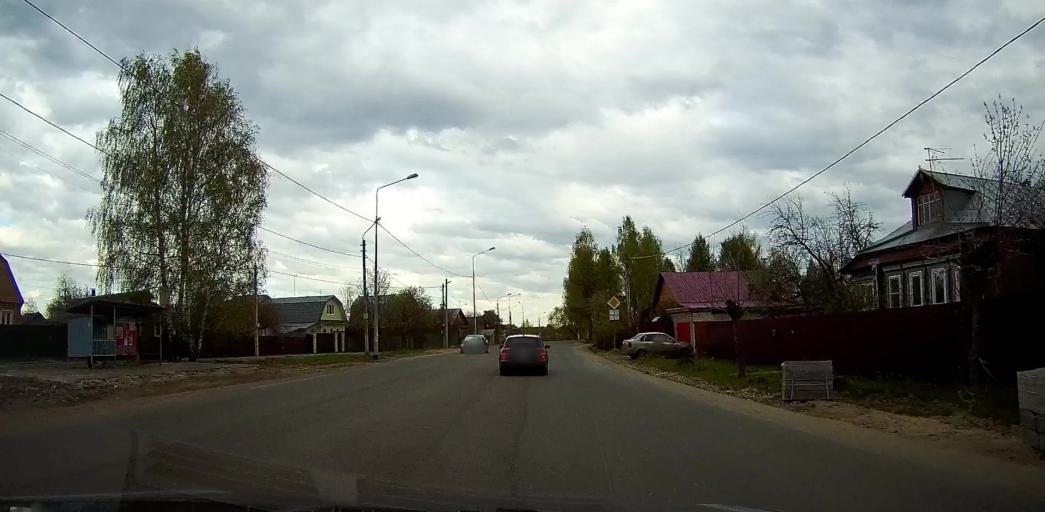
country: RU
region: Moskovskaya
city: Pavlovskiy Posad
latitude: 55.7683
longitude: 38.6955
